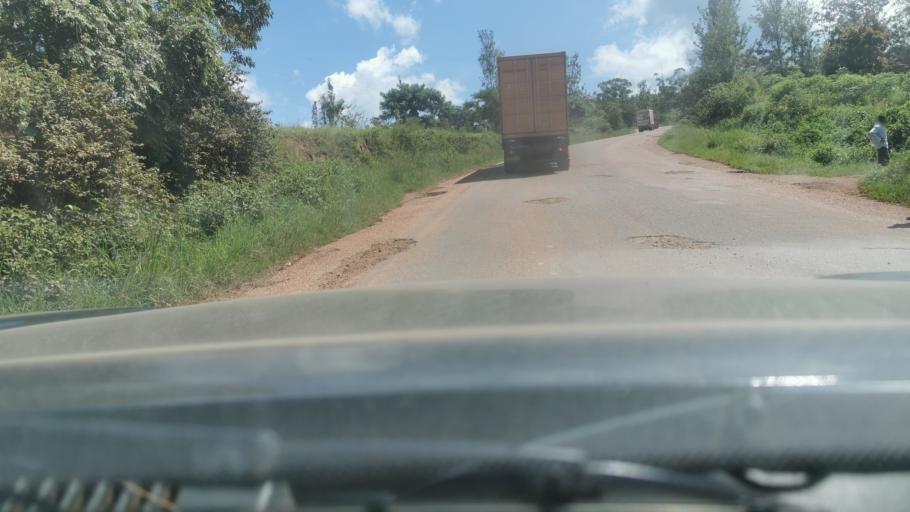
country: TZ
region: Kagera
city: Ngara
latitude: -2.3838
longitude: 30.7884
